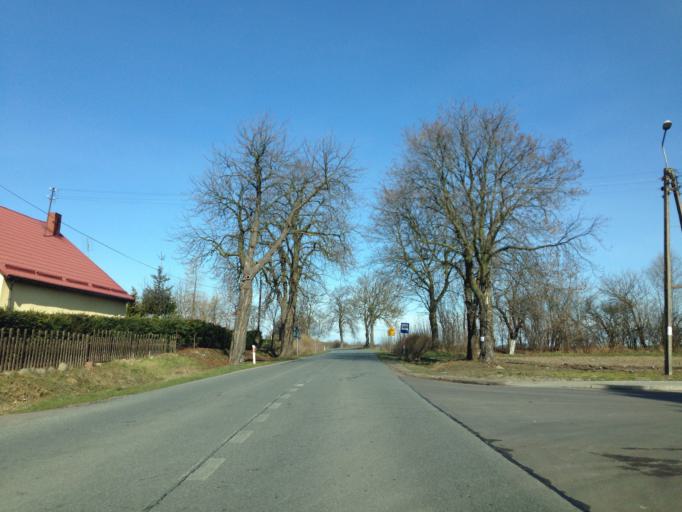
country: PL
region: Pomeranian Voivodeship
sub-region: Powiat malborski
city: Malbork
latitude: 53.9932
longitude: 19.1038
